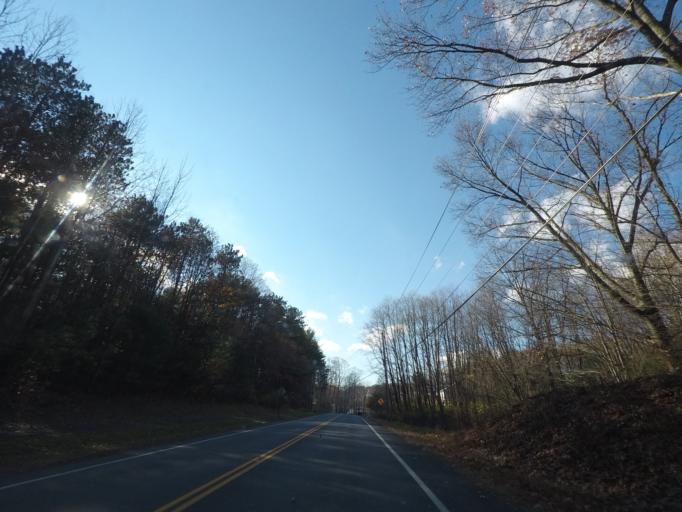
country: US
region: New York
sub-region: Saratoga County
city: Country Knolls
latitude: 42.8887
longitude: -73.8087
